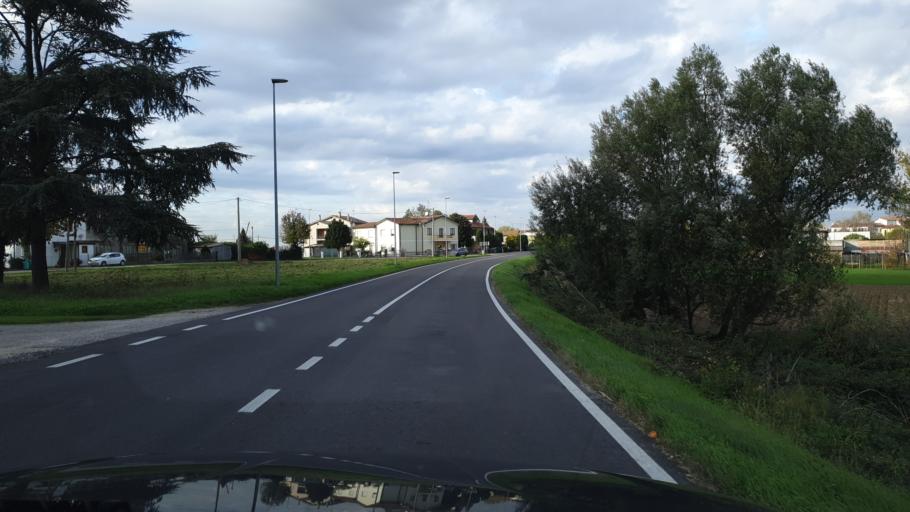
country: IT
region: Veneto
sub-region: Provincia di Rovigo
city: Villanova del Ghebbo Canton
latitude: 45.0486
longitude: 11.6460
